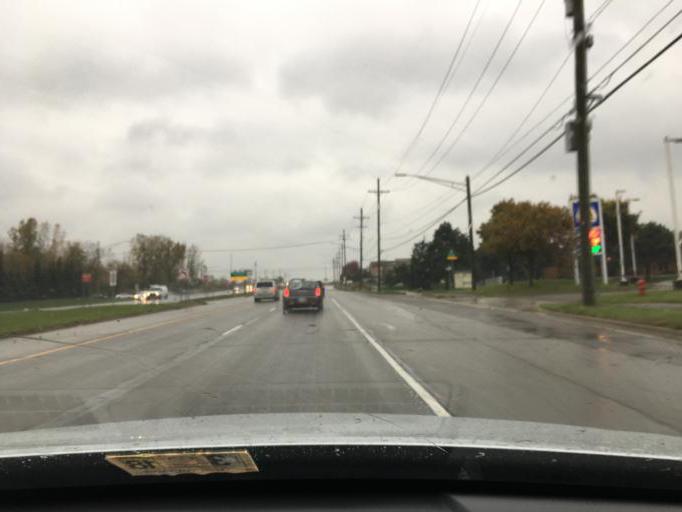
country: US
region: Michigan
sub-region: Oakland County
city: Auburn Hills
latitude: 42.6990
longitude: -83.2421
